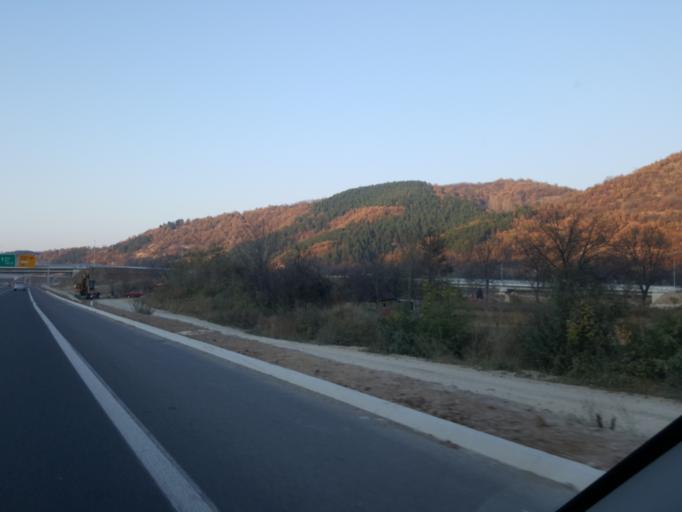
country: RS
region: Central Serbia
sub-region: Pirotski Okrug
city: Pirot
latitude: 43.1847
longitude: 22.5659
